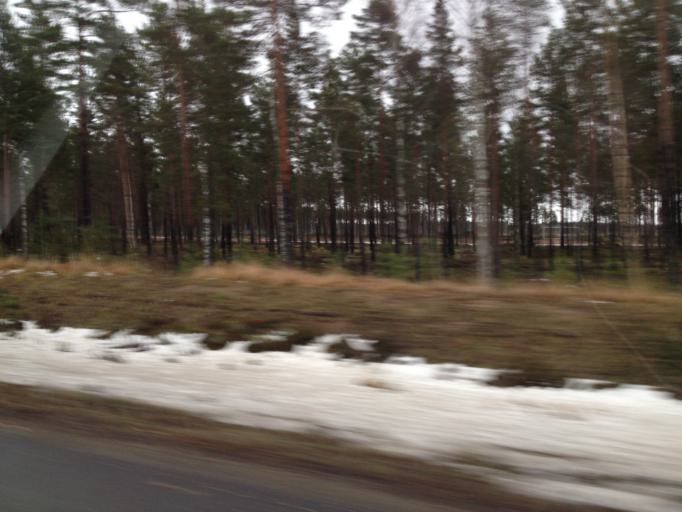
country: FI
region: Uusimaa
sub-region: Raaseporin
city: Hanko
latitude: 59.8536
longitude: 23.0124
